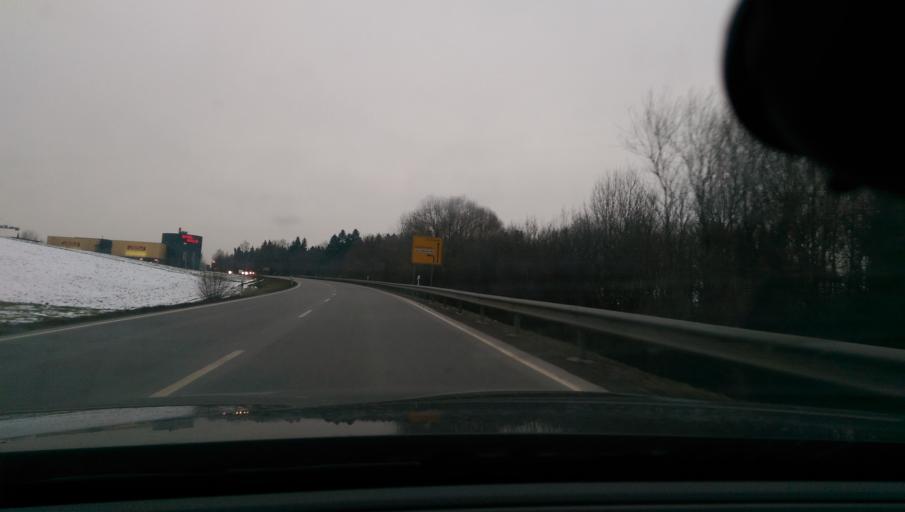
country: DE
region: Bavaria
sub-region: Lower Bavaria
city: Salzweg
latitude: 48.6443
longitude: 13.4763
